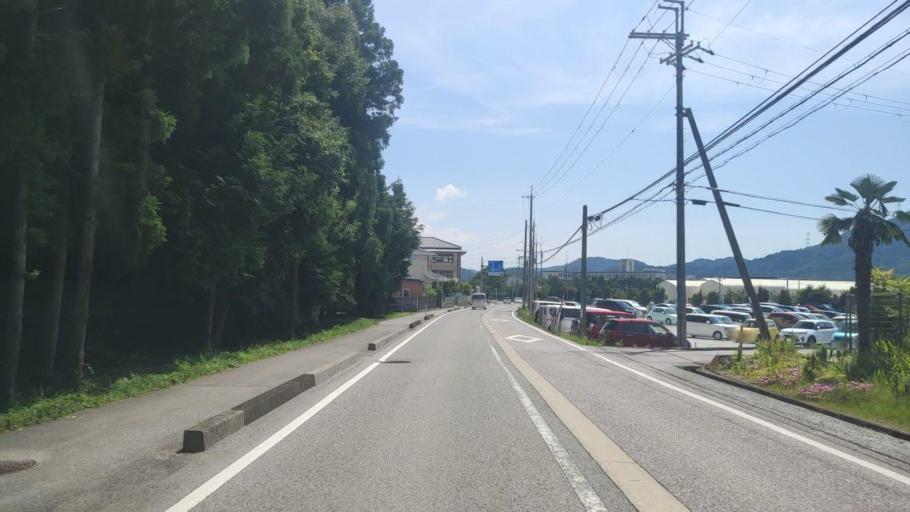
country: JP
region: Shiga Prefecture
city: Nagahama
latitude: 35.3854
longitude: 136.3542
